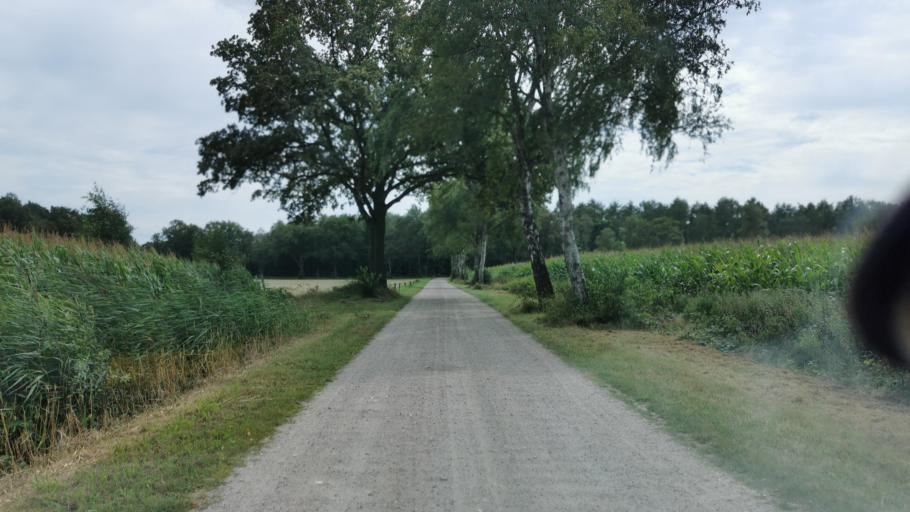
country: NL
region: Overijssel
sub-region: Gemeente Losser
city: Losser
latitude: 52.2509
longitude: 6.9567
